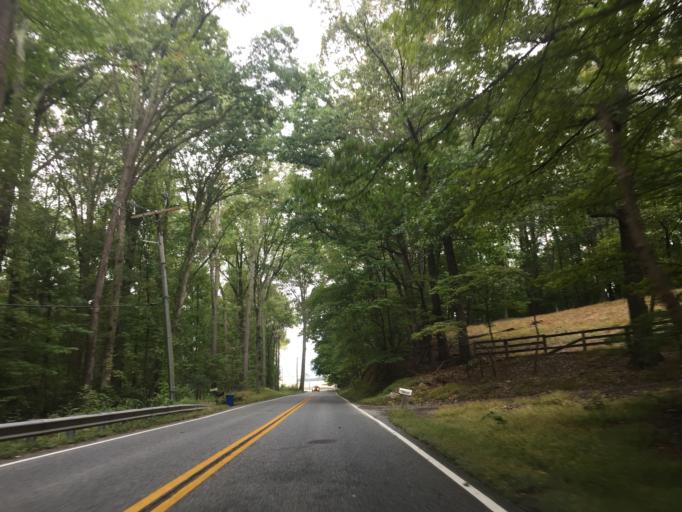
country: US
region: Maryland
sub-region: Baltimore County
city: Owings Mills
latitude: 39.4722
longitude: -76.7573
